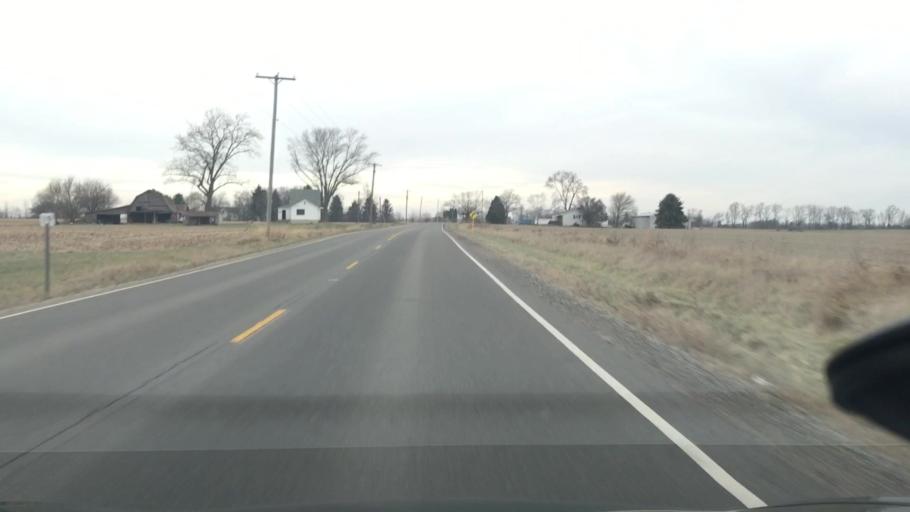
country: US
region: Ohio
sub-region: Madison County
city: Mount Sterling
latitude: 39.7700
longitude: -83.3144
